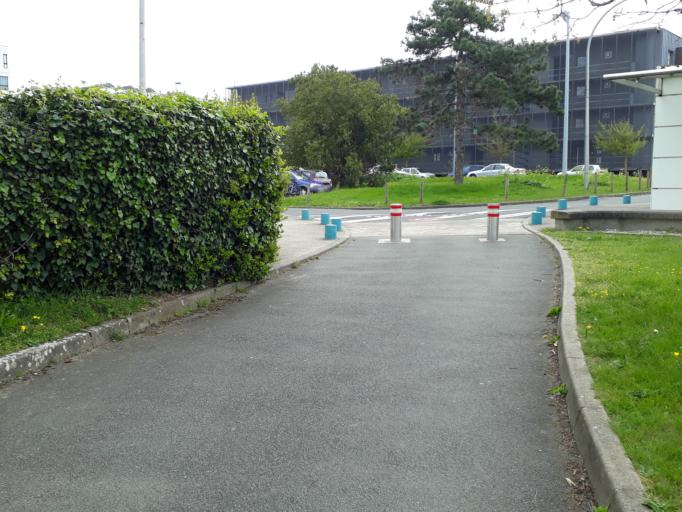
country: FR
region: Poitou-Charentes
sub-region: Departement de la Charente-Maritime
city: La Rochelle
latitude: 46.1414
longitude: -1.1521
